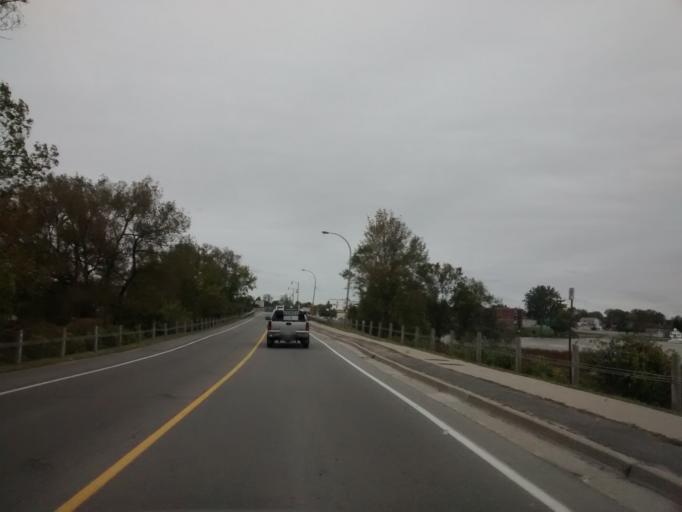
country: CA
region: Ontario
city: Welland
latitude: 42.8982
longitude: -79.6211
